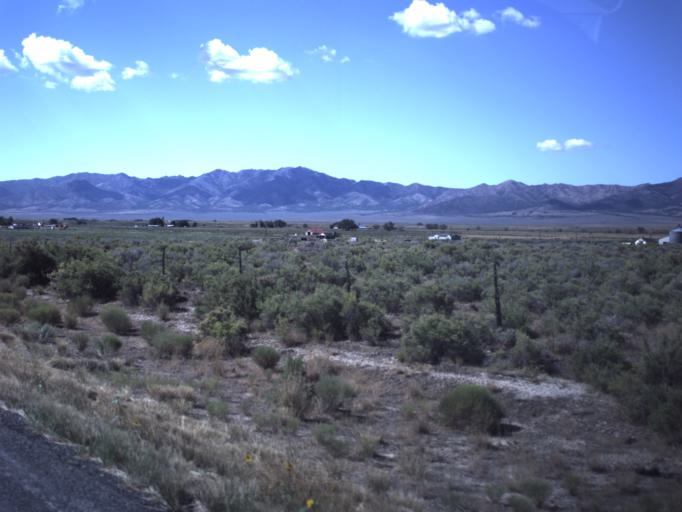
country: US
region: Utah
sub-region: Tooele County
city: Tooele
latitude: 40.1172
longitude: -112.4308
